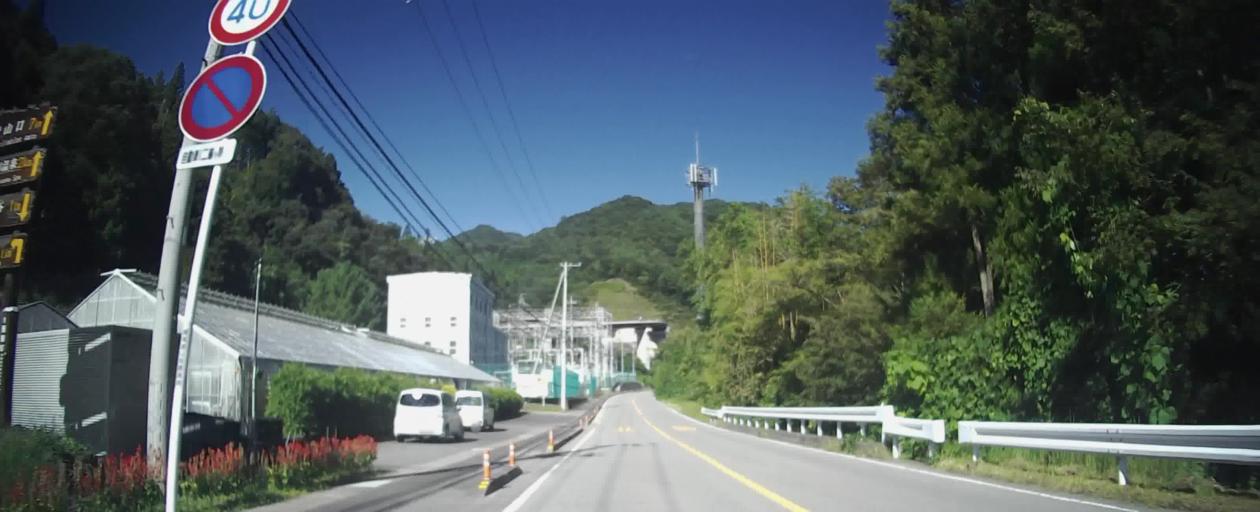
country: JP
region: Gunma
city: Nakanojomachi
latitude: 36.5705
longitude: 138.7323
